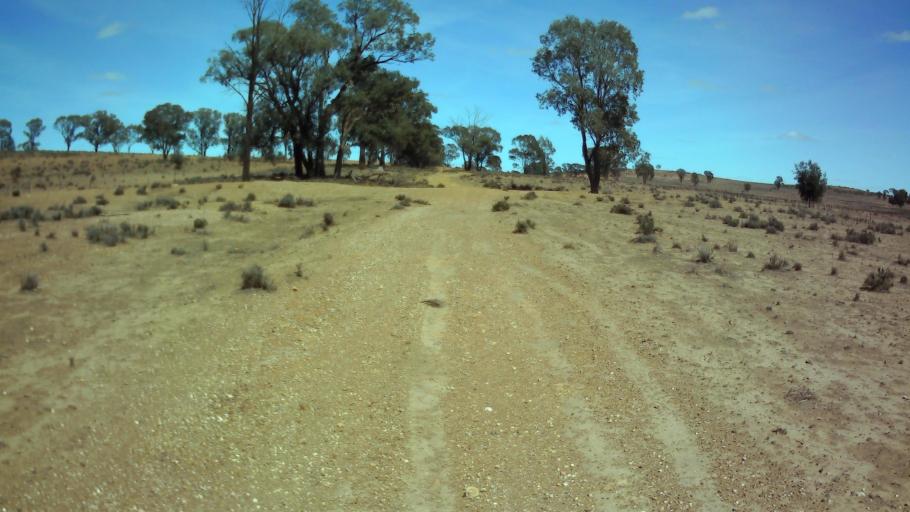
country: AU
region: New South Wales
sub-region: Weddin
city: Grenfell
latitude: -33.7205
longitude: 147.8388
